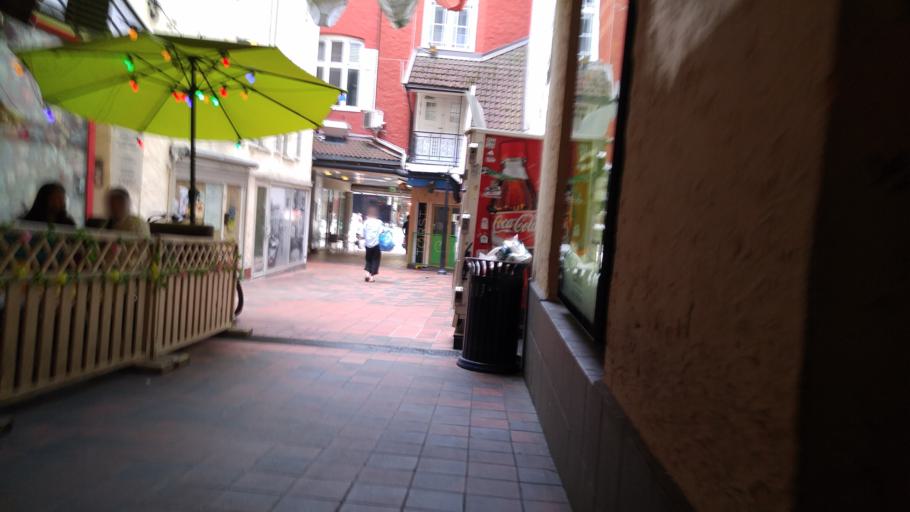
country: NO
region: Oslo
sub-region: Oslo
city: Oslo
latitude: 59.9137
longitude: 10.7489
